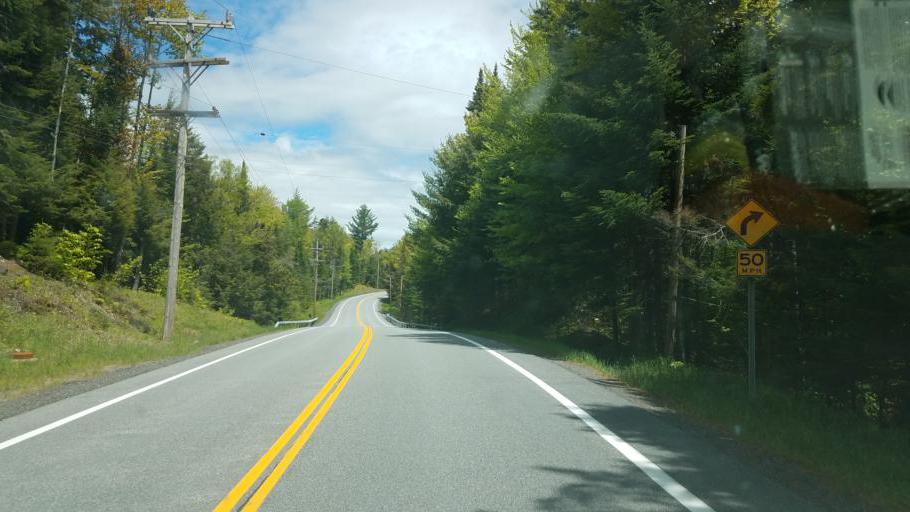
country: US
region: New York
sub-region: Hamilton County
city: Lake Pleasant
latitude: 43.8130
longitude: -74.5960
